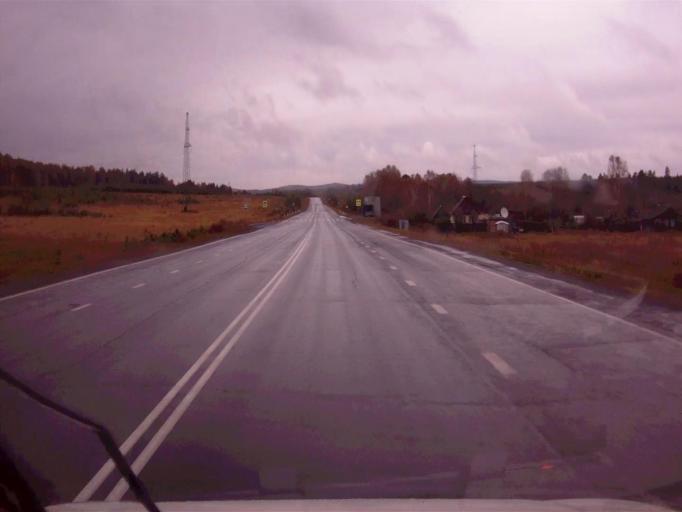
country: RU
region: Chelyabinsk
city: Verkhniy Ufaley
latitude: 56.0046
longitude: 60.3277
